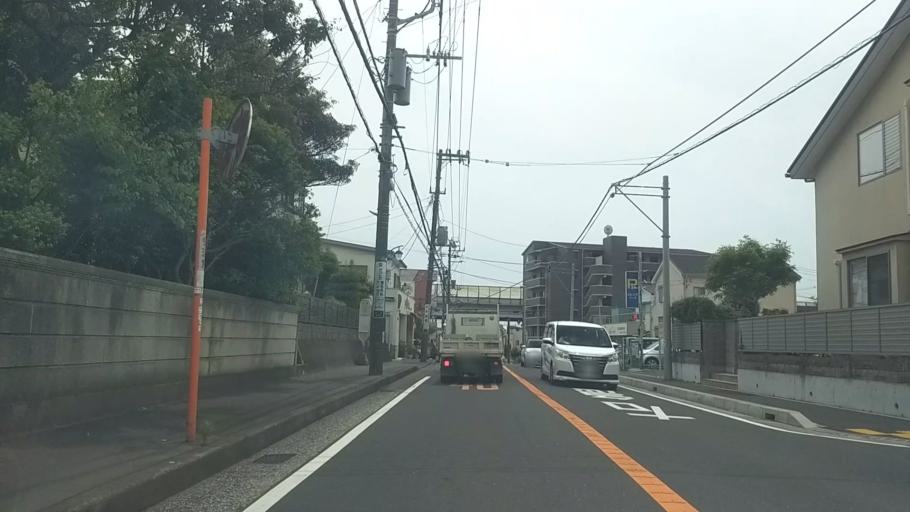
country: JP
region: Kanagawa
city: Chigasaki
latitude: 35.3514
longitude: 139.4153
